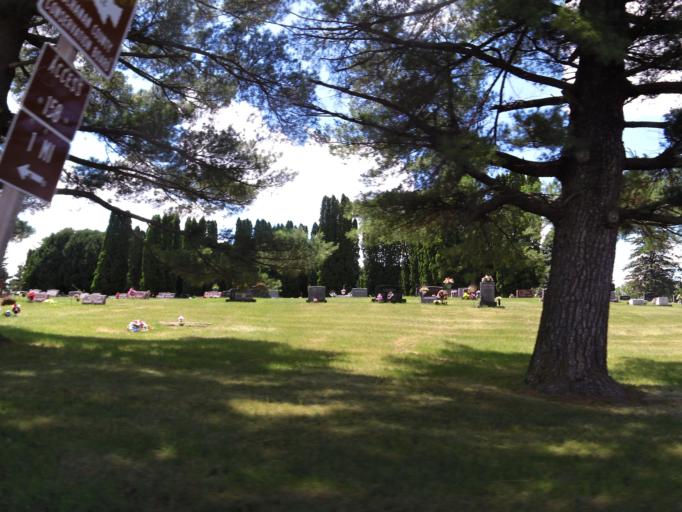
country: US
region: Iowa
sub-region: Buchanan County
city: Independence
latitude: 42.4572
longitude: -91.8903
